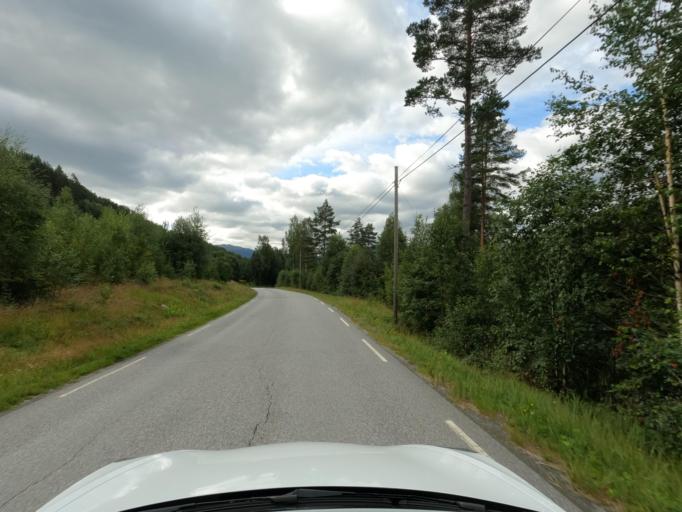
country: NO
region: Telemark
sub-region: Tinn
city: Rjukan
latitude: 60.0083
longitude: 8.8351
